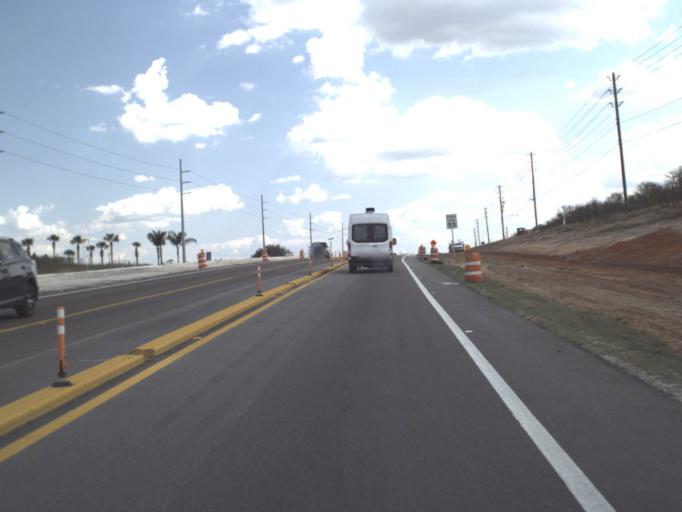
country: US
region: Florida
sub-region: Lake County
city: Four Corners
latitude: 28.4122
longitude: -81.7017
